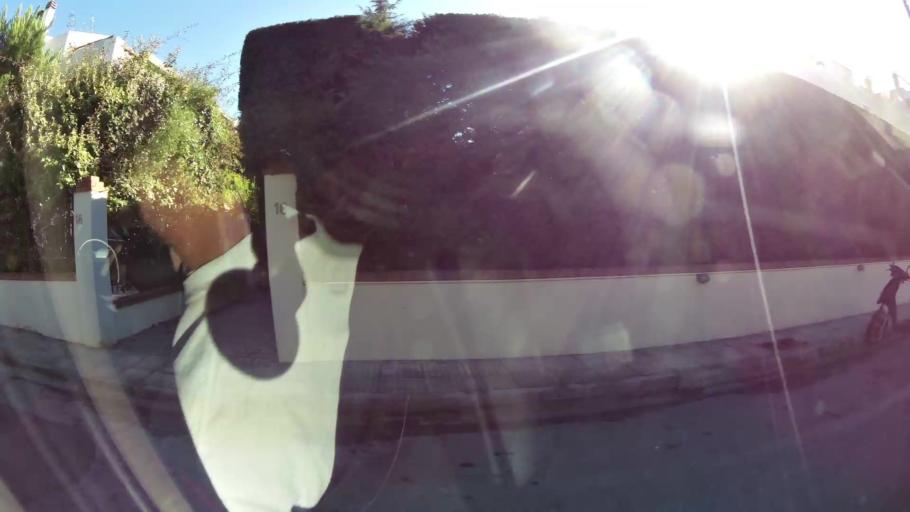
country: GR
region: Attica
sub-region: Nomarchia Anatolikis Attikis
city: Vari
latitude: 37.8360
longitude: 23.8097
